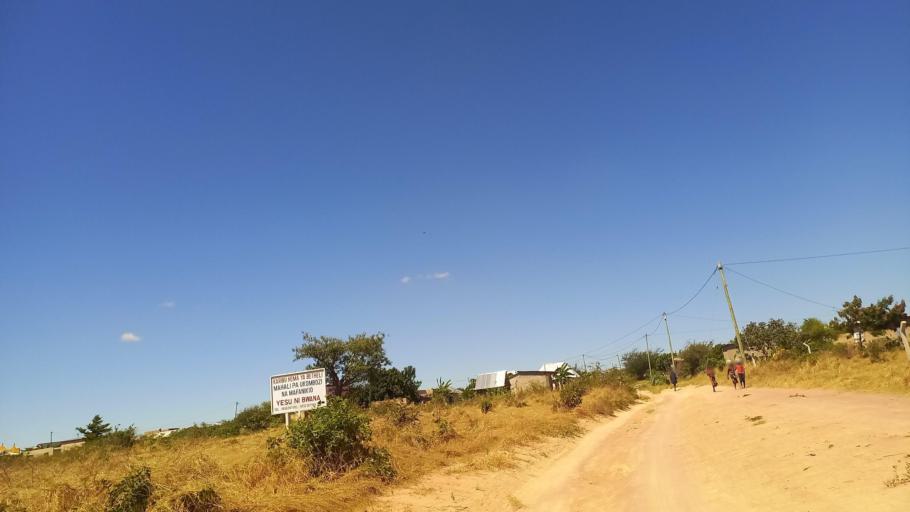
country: TZ
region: Dodoma
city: Dodoma
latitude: -6.1270
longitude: 35.6966
